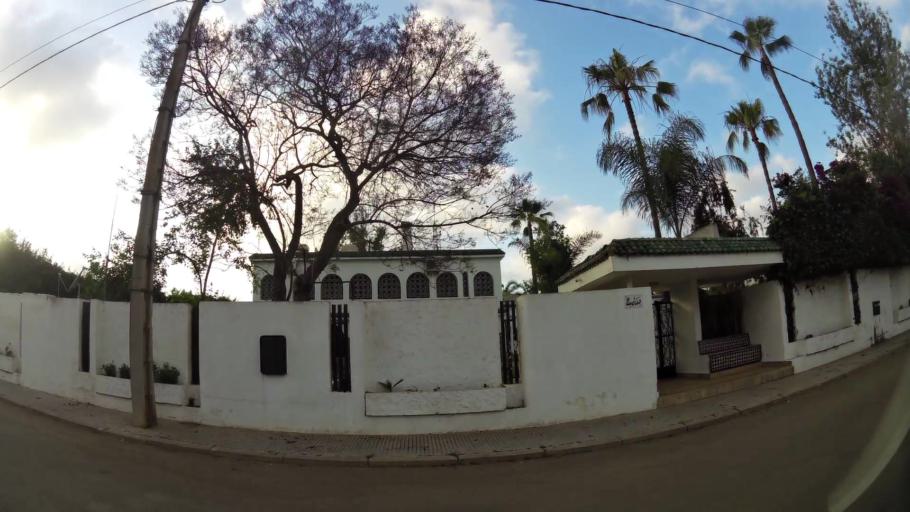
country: MA
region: Rabat-Sale-Zemmour-Zaer
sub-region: Rabat
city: Rabat
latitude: 33.9592
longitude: -6.8295
